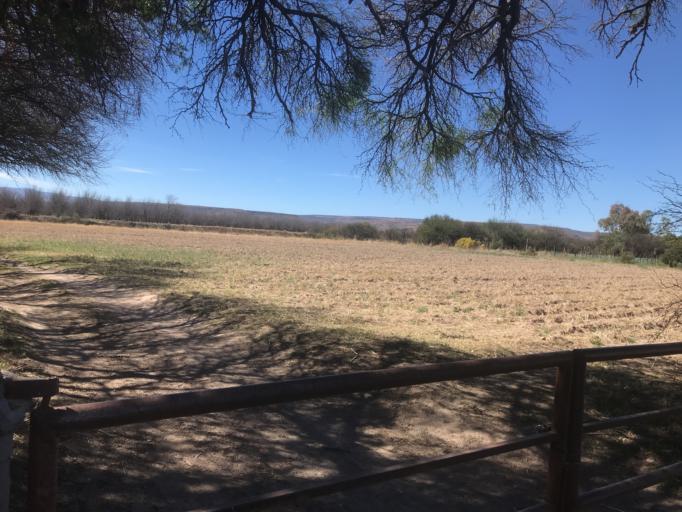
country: MX
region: Durango
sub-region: Durango
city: Sebastian Lerdo de Tejada
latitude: 23.9752
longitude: -104.6211
